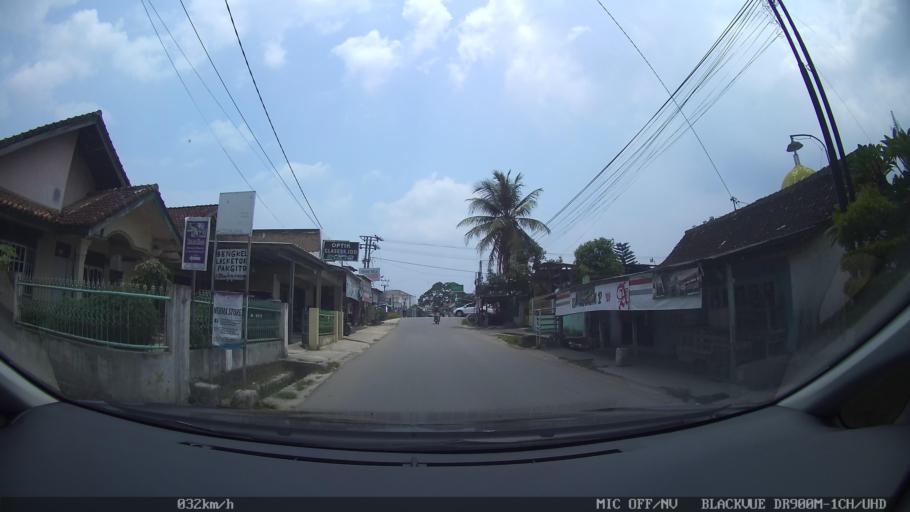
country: ID
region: Lampung
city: Pringsewu
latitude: -5.3535
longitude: 104.9798
